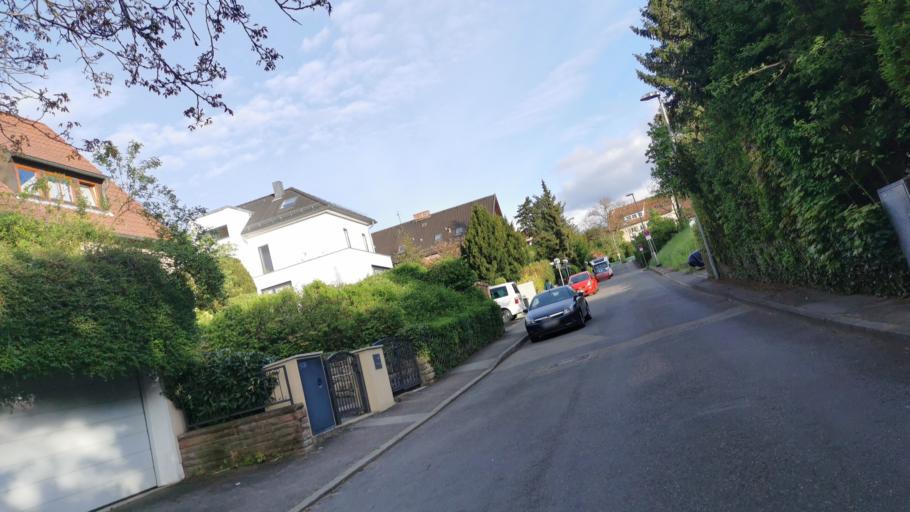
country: DE
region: Baden-Wuerttemberg
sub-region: Regierungsbezirk Stuttgart
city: Korntal
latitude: 48.8246
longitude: 9.1231
